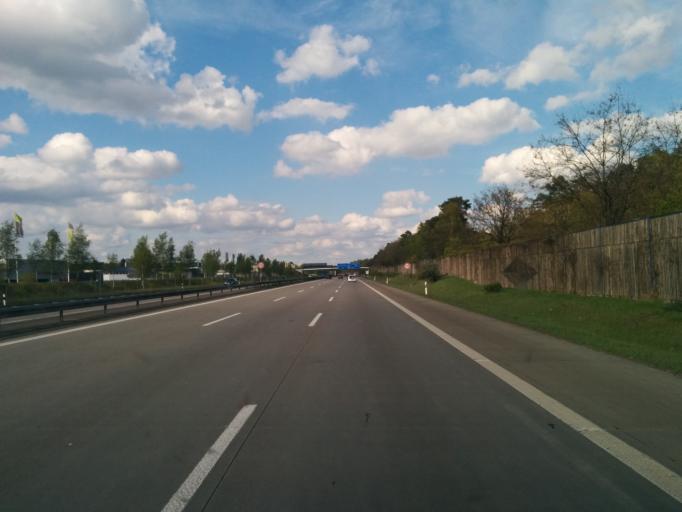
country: DE
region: Berlin
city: Nikolassee
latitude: 52.4041
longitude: 13.1894
